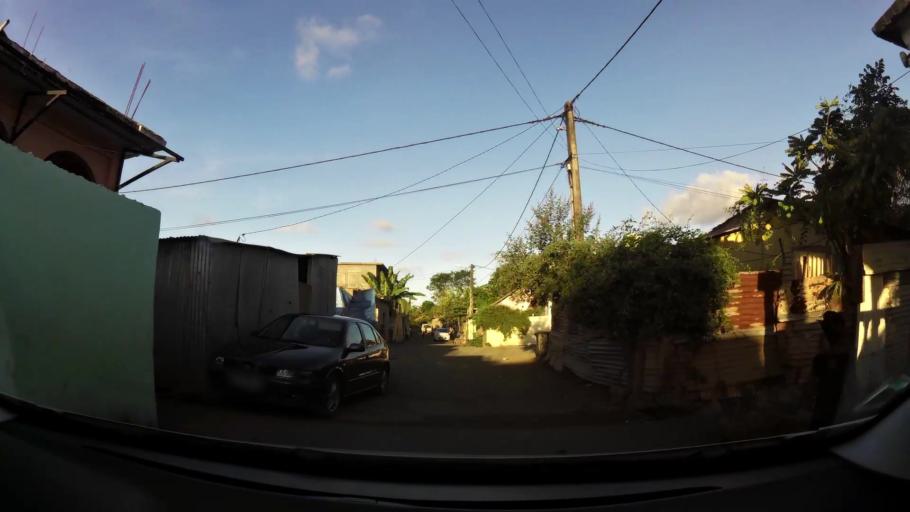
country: YT
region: Dembeni
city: Dembeni
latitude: -12.8441
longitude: 45.1851
